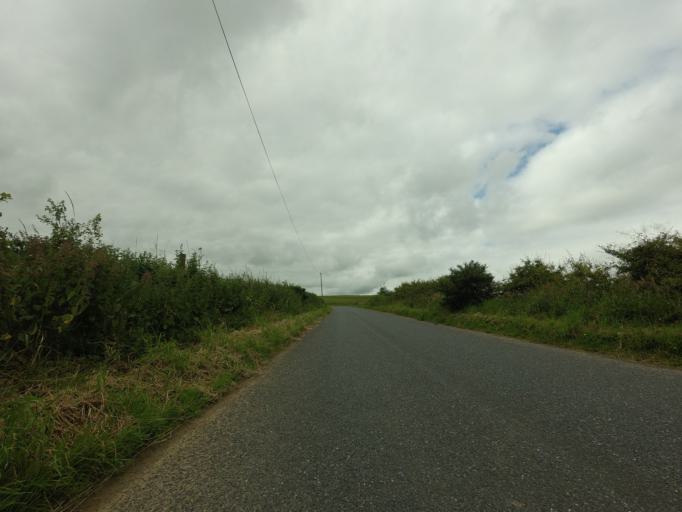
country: GB
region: Scotland
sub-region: Aberdeenshire
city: Rosehearty
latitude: 57.5403
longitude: -2.1956
